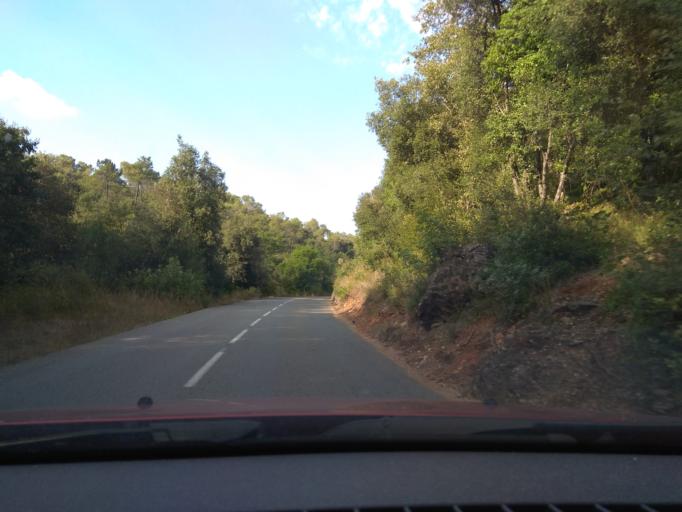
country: FR
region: Provence-Alpes-Cote d'Azur
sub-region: Departement des Alpes-Maritimes
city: Tourrettes-sur-Loup
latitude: 43.6808
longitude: 7.0516
